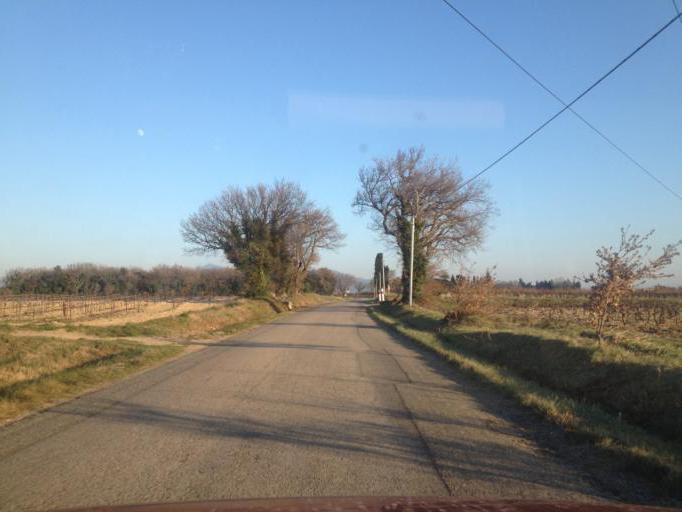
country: FR
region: Provence-Alpes-Cote d'Azur
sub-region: Departement du Vaucluse
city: Camaret-sur-Aigues
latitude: 44.1617
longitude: 4.9027
